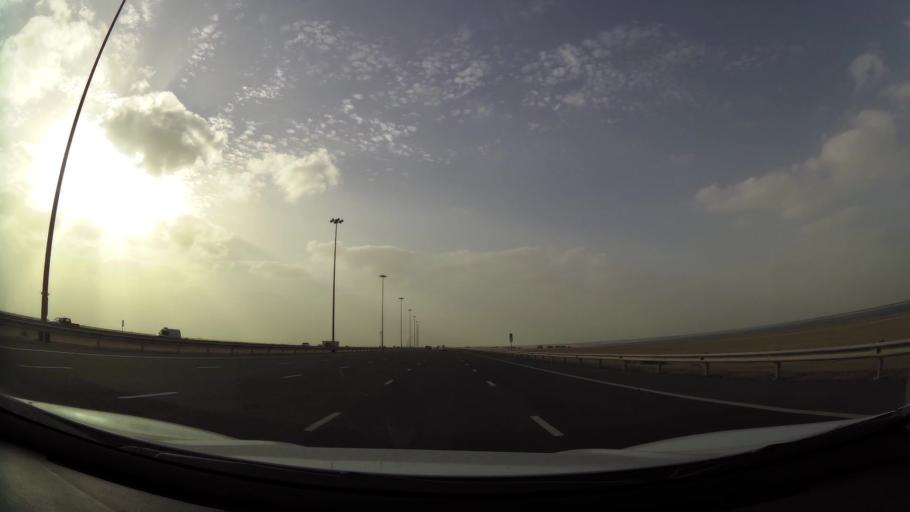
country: AE
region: Abu Dhabi
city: Abu Dhabi
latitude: 24.5133
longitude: 54.5445
